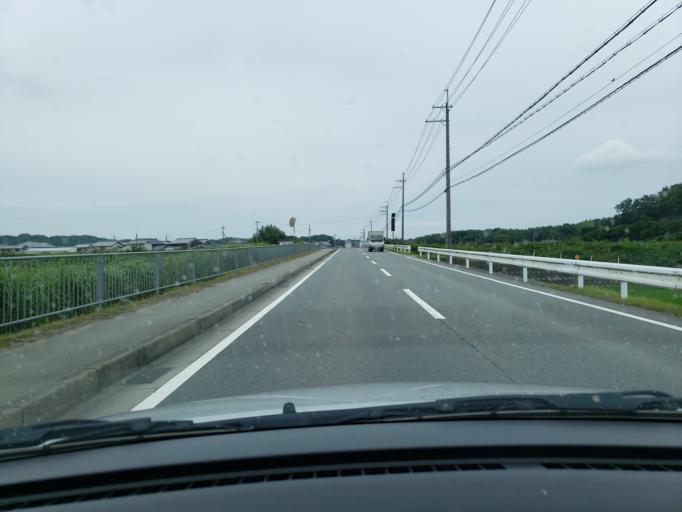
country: JP
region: Hyogo
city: Ono
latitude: 34.7904
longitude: 134.9011
